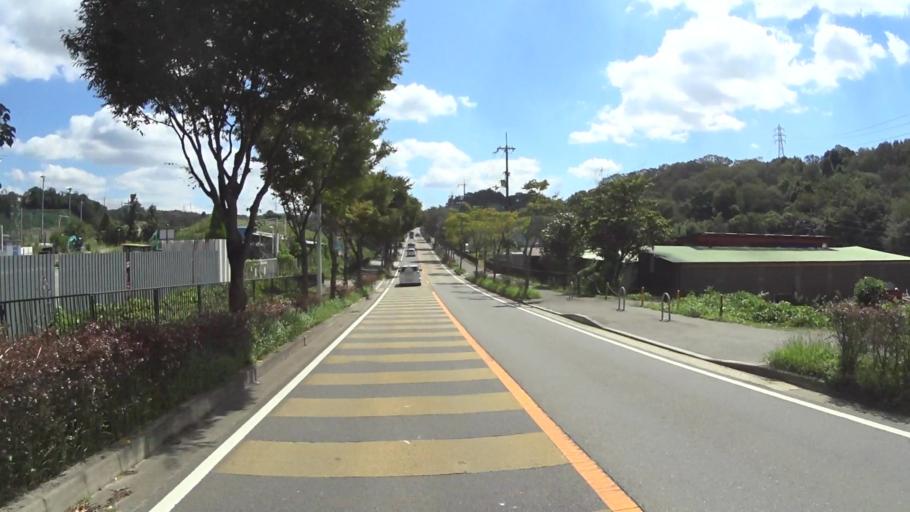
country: JP
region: Kyoto
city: Uji
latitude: 34.8632
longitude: 135.7973
